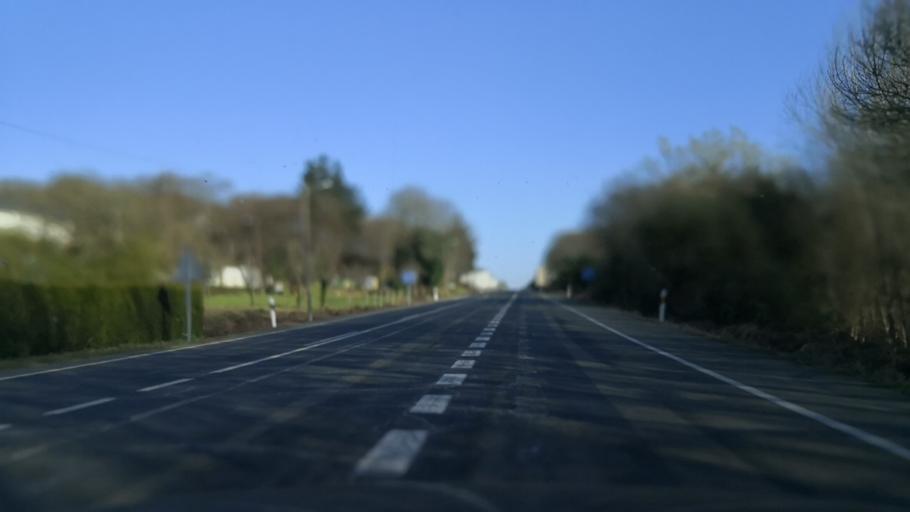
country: ES
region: Galicia
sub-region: Provincia de Lugo
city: Corgo
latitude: 42.9601
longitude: -7.4766
